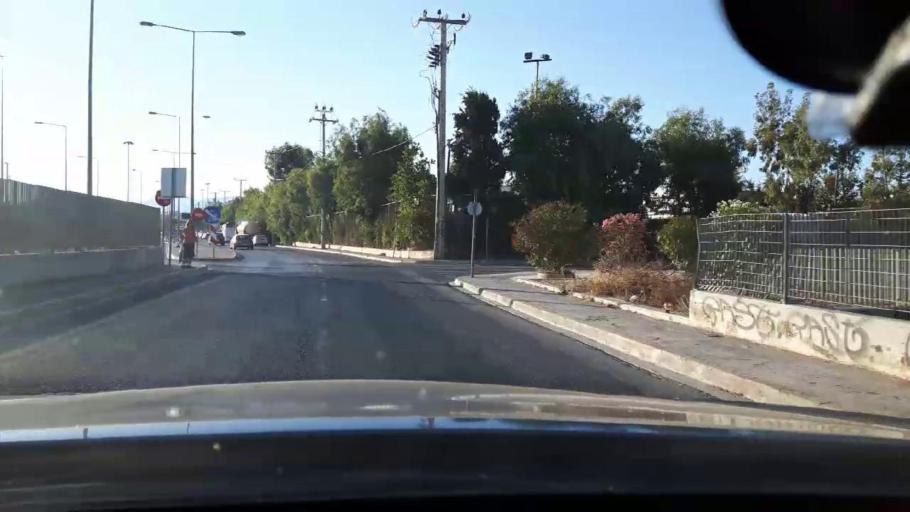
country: GR
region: Attica
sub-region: Nomarchia Athinas
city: Vrilissia
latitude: 38.0321
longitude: 23.8243
